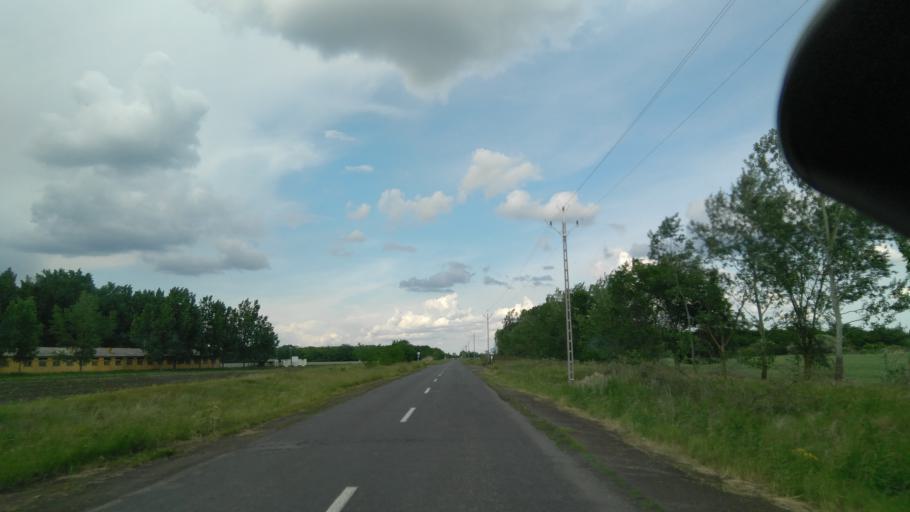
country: HU
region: Bekes
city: Dombegyhaz
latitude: 46.3310
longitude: 21.1019
